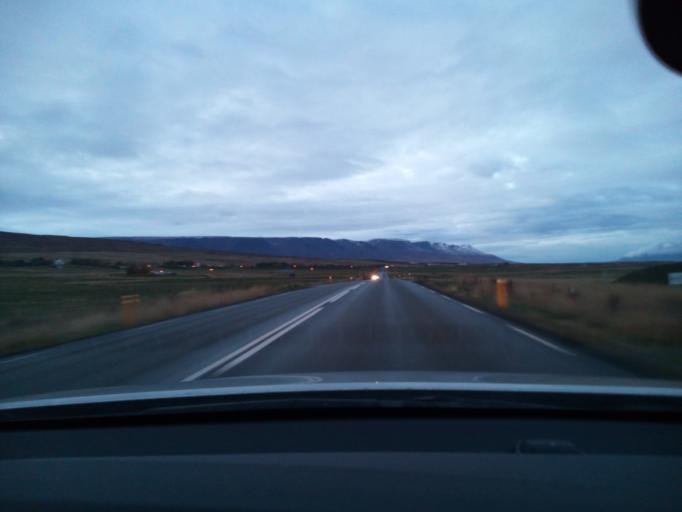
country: IS
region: Northeast
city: Akureyri
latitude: 65.7130
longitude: -18.1662
